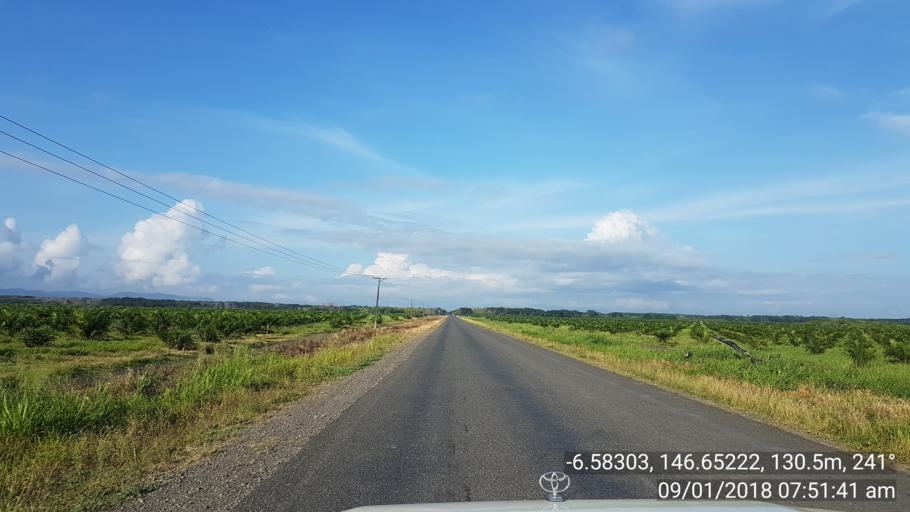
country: PG
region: Morobe
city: Lae
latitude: -6.5831
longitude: 146.6522
